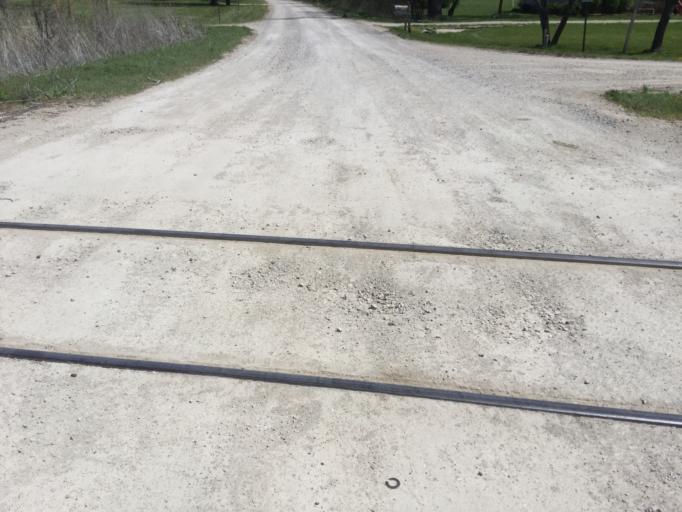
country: US
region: Kansas
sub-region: Montgomery County
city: Cherryvale
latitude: 37.3840
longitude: -95.5091
